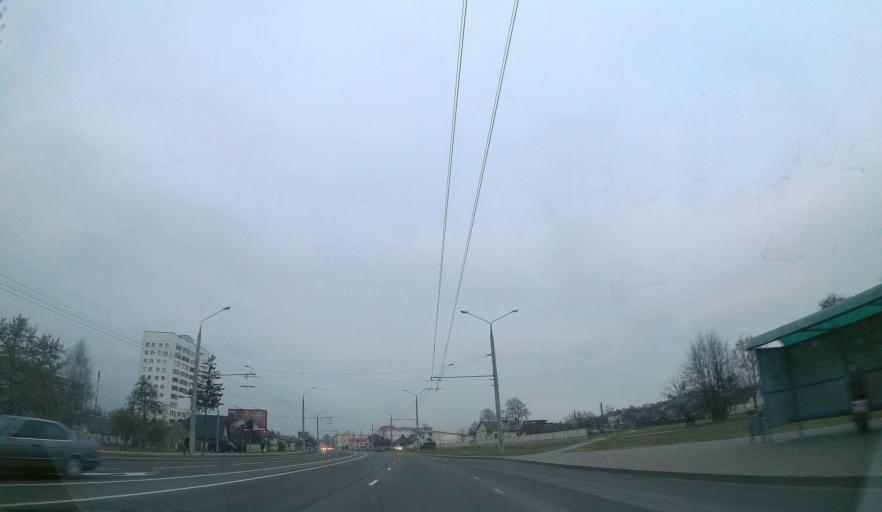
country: BY
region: Grodnenskaya
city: Hrodna
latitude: 53.6617
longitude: 23.8167
